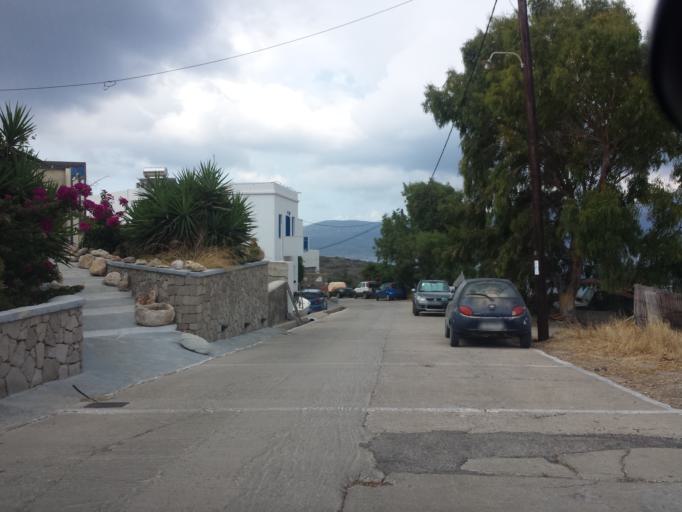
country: GR
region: South Aegean
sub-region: Nomos Kykladon
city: Milos
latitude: 36.7395
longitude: 24.4243
